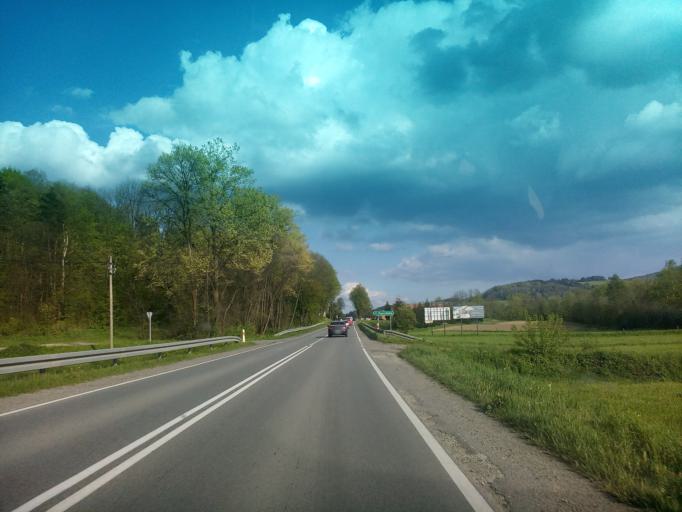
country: PL
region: Lesser Poland Voivodeship
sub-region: Powiat nowosadecki
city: Nawojowa
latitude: 49.5477
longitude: 20.7789
